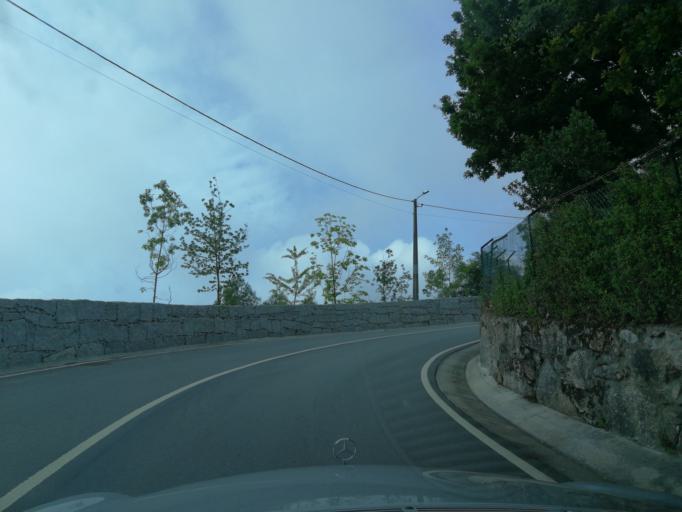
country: PT
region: Braga
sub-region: Braga
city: Braga
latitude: 41.5172
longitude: -8.3712
